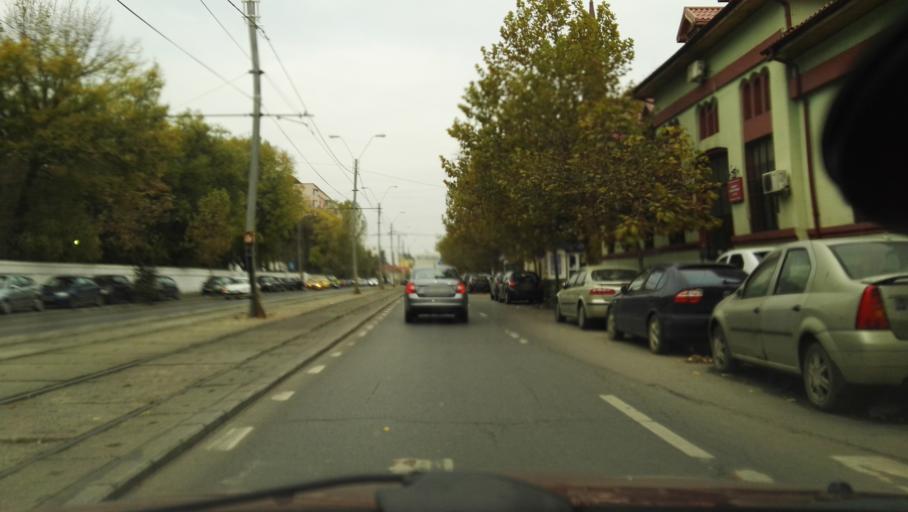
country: RO
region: Bucuresti
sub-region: Municipiul Bucuresti
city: Bucuresti
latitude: 44.4069
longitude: 26.0936
